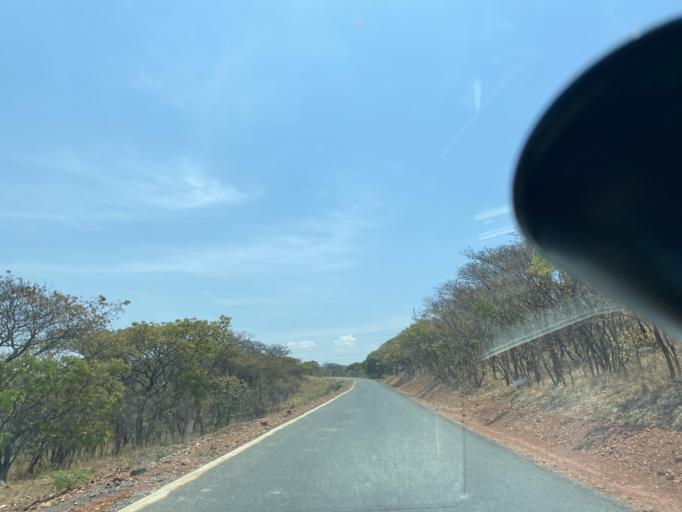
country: ZM
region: Lusaka
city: Kafue
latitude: -15.8554
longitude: 28.4187
